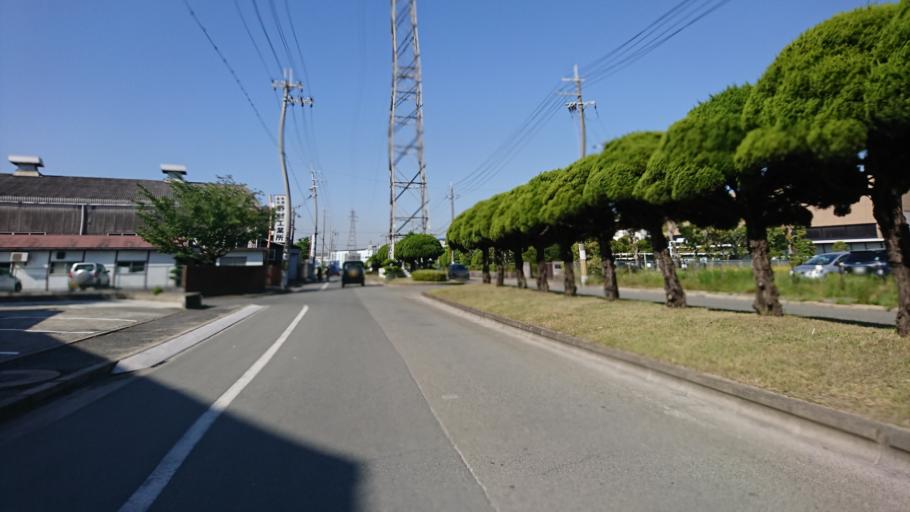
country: JP
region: Hyogo
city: Kakogawacho-honmachi
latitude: 34.7634
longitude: 134.8686
